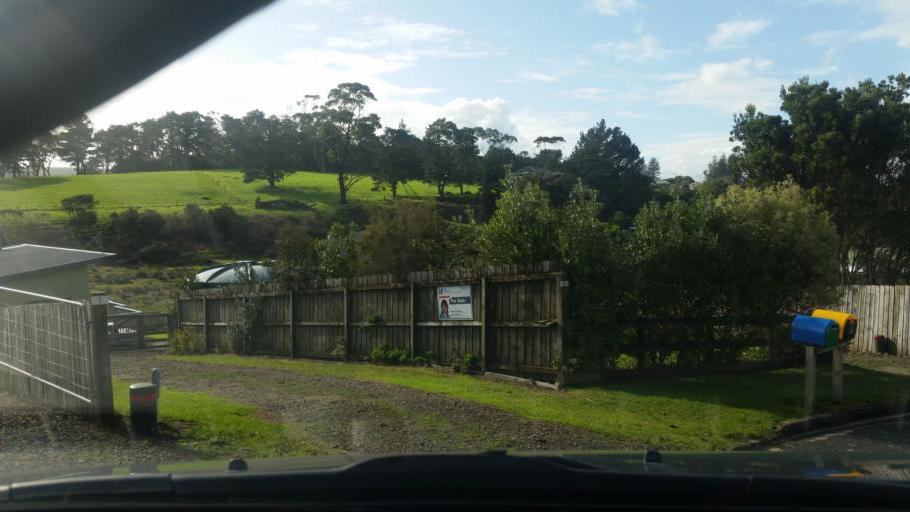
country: NZ
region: Auckland
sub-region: Auckland
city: Wellsford
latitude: -36.2546
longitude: 174.2438
